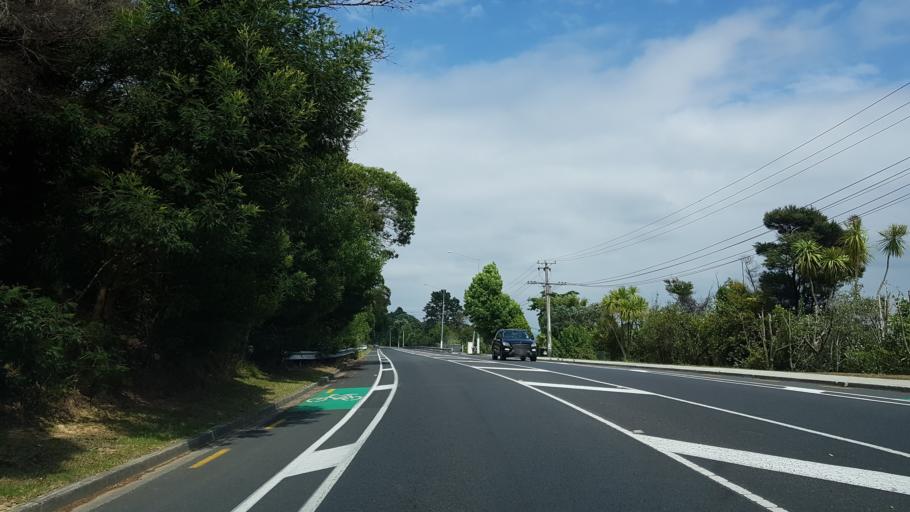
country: NZ
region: Auckland
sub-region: Auckland
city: North Shore
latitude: -36.7780
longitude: 174.6863
